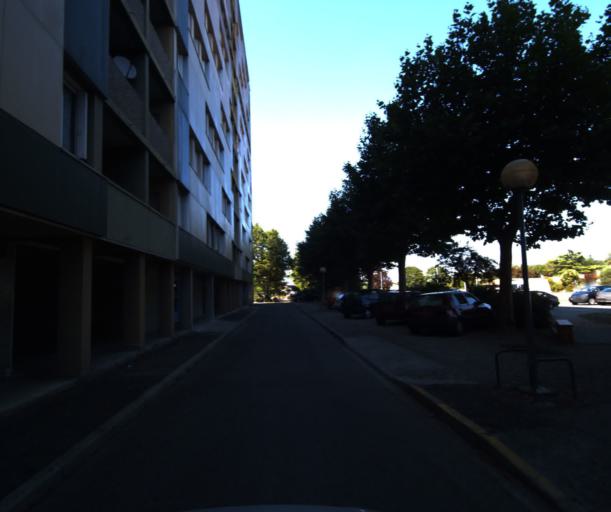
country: FR
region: Midi-Pyrenees
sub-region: Departement de la Haute-Garonne
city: Muret
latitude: 43.4696
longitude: 1.3361
